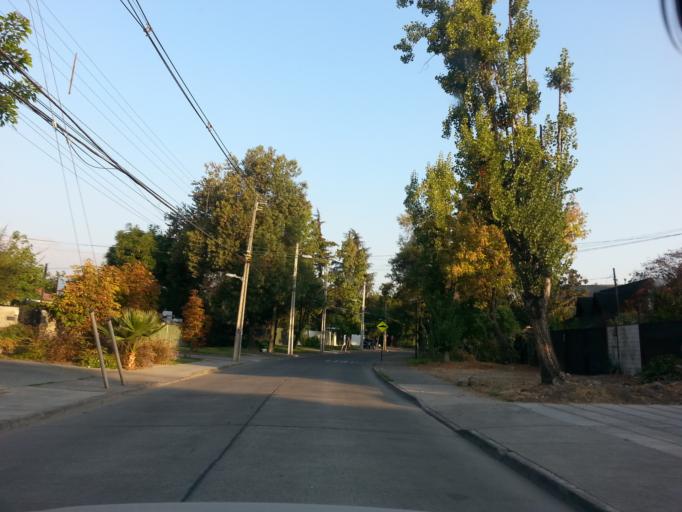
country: CL
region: Santiago Metropolitan
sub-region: Provincia de Santiago
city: Villa Presidente Frei, Nunoa, Santiago, Chile
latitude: -33.3814
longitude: -70.5741
